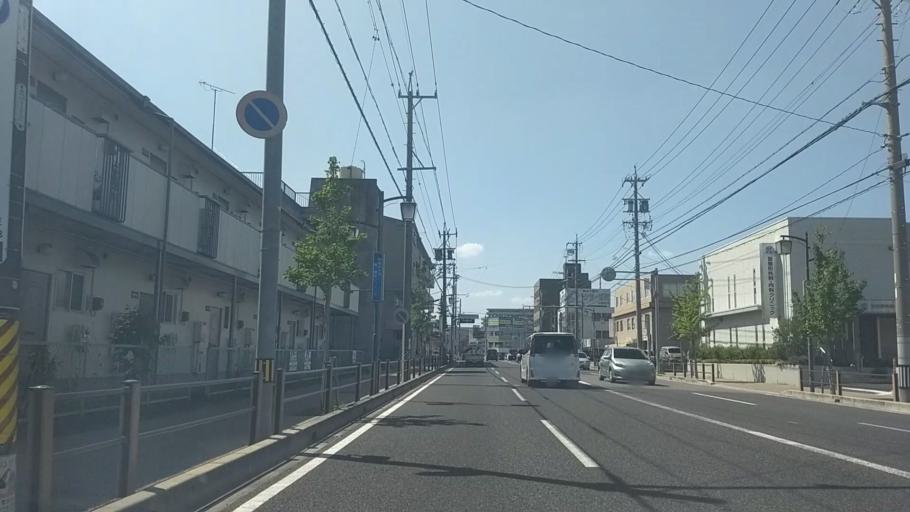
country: JP
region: Aichi
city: Okazaki
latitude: 34.9707
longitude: 137.1725
